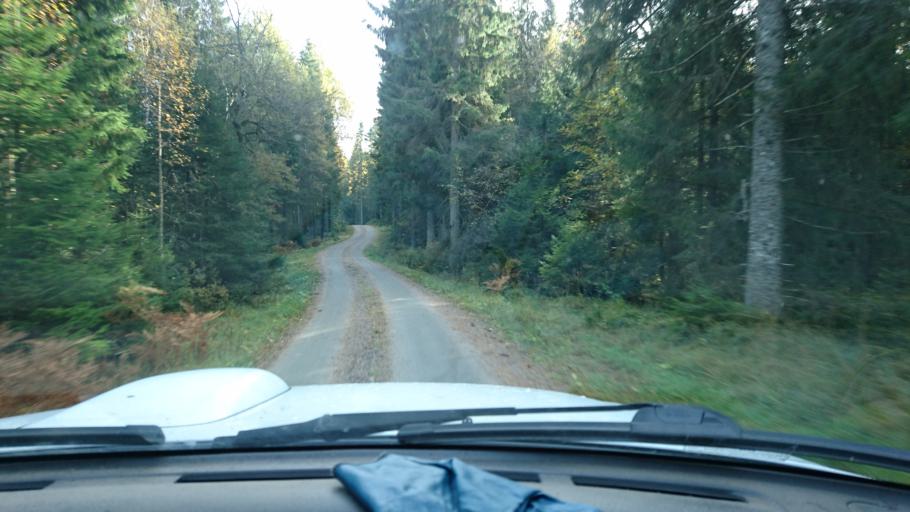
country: SE
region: Vaestra Goetaland
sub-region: Ulricehamns Kommun
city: Ulricehamn
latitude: 57.9434
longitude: 13.5427
